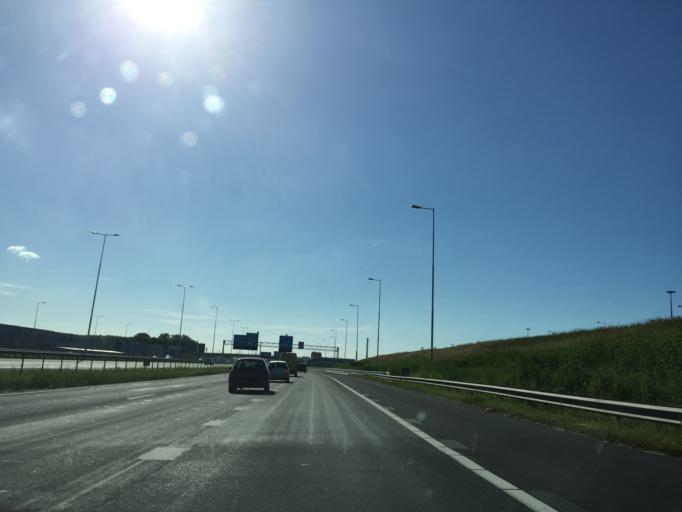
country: NL
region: South Holland
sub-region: Gemeente Albrandswaard
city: Rhoon
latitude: 51.8727
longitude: 4.4209
